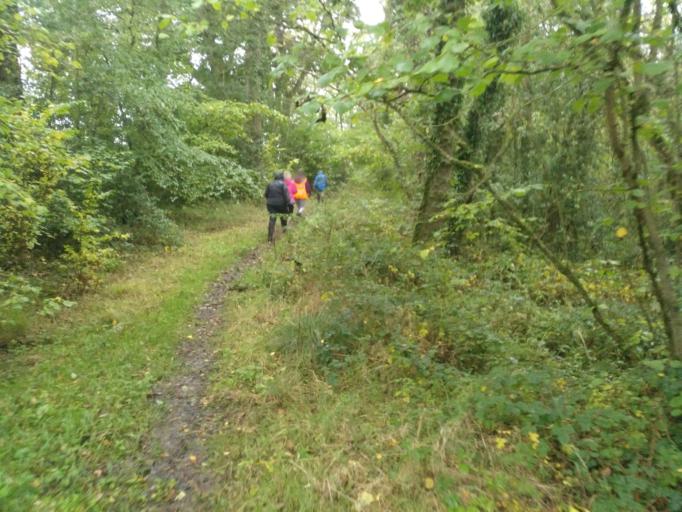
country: IE
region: Leinster
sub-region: Kilkenny
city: Castlecomer
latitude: 52.7911
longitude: -7.1961
